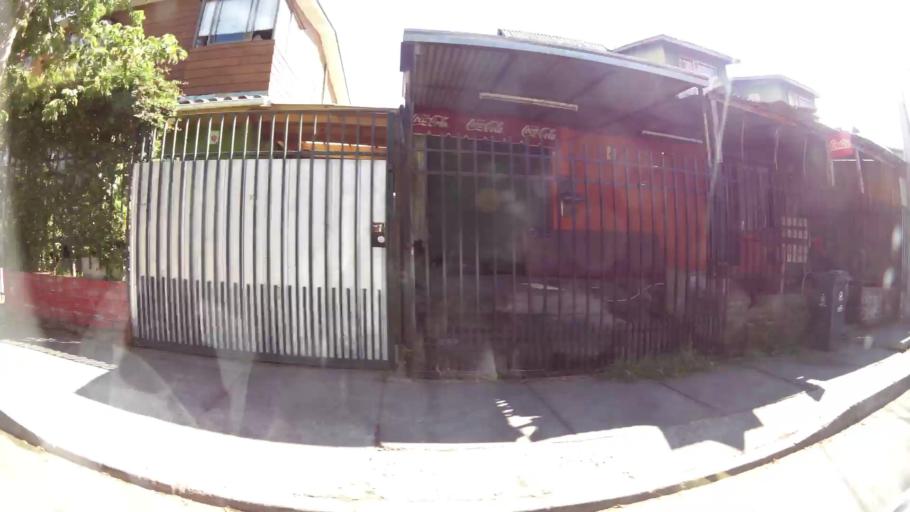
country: CL
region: Maule
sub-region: Provincia de Curico
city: Curico
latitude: -34.9780
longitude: -71.2611
